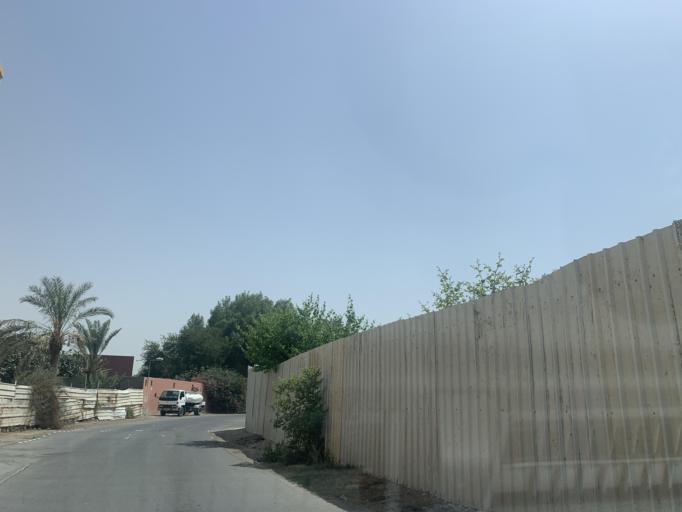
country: BH
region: Central Governorate
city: Madinat Hamad
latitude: 26.1512
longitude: 50.4968
